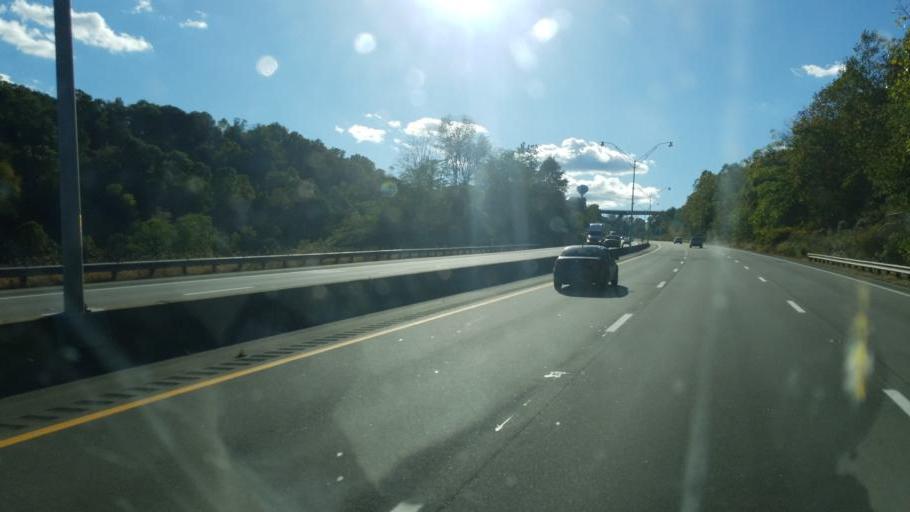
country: US
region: West Virginia
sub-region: Ohio County
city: Bethlehem
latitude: 40.0506
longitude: -80.6814
